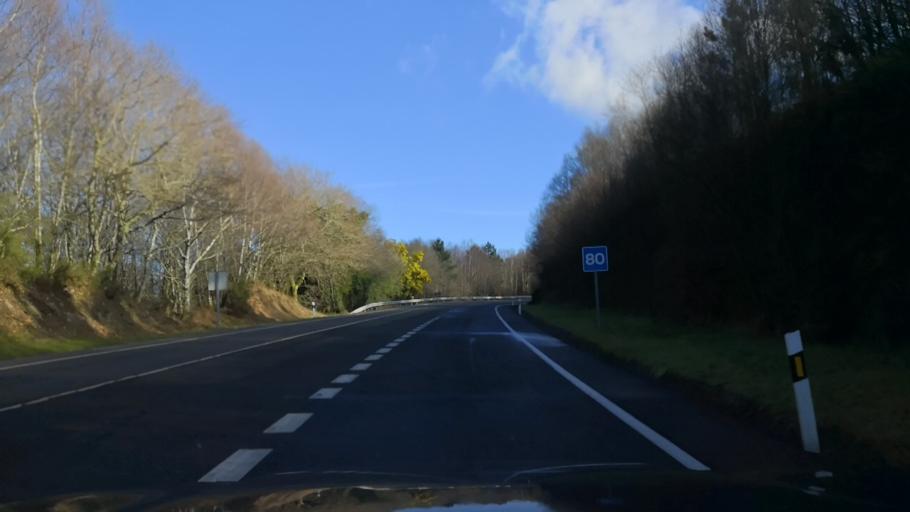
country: ES
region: Galicia
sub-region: Provincia da Coruna
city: Ribeira
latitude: 42.7149
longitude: -8.3619
